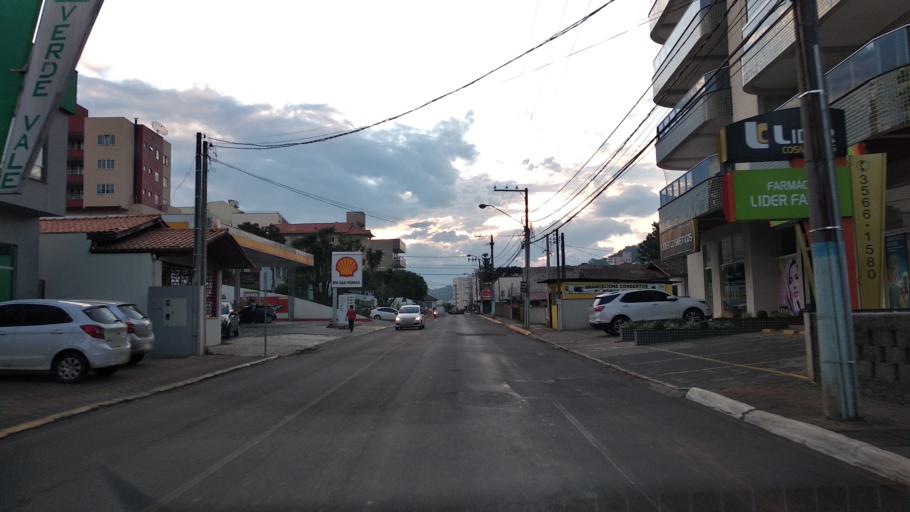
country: BR
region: Santa Catarina
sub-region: Videira
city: Videira
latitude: -27.0058
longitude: -51.1443
